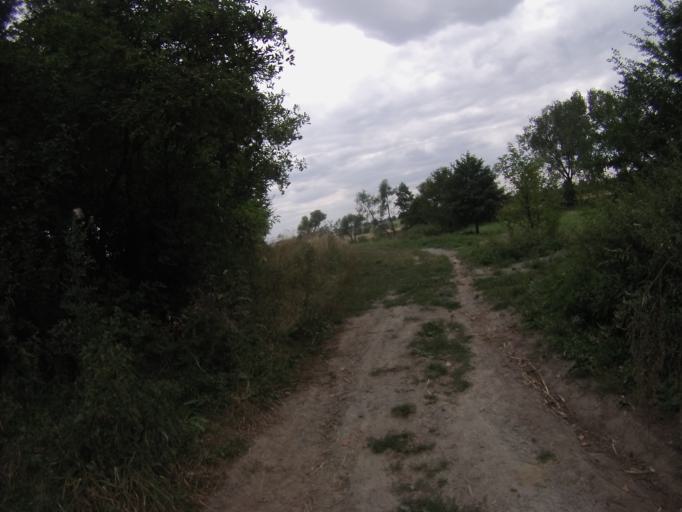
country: PL
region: Swietokrzyskie
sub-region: Powiat staszowski
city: Bogoria
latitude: 50.6861
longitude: 21.2452
